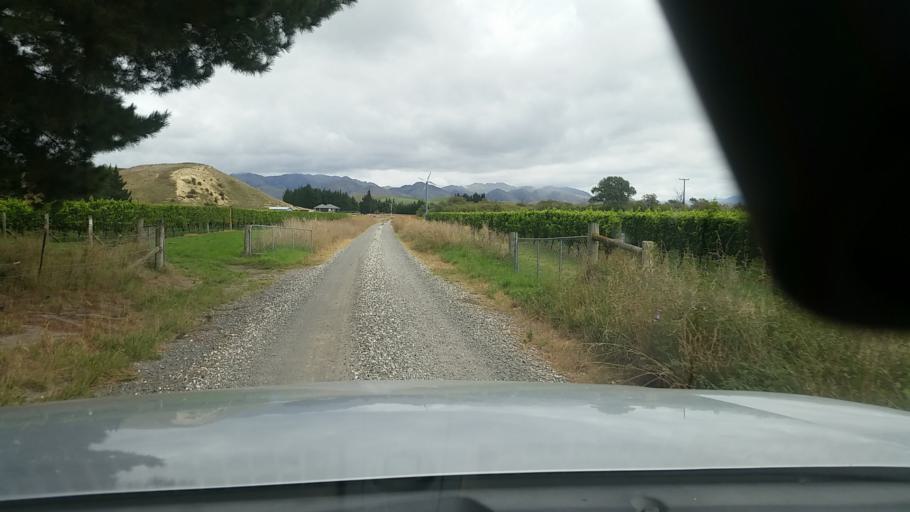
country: NZ
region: Marlborough
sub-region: Marlborough District
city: Blenheim
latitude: -41.6959
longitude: 174.1236
